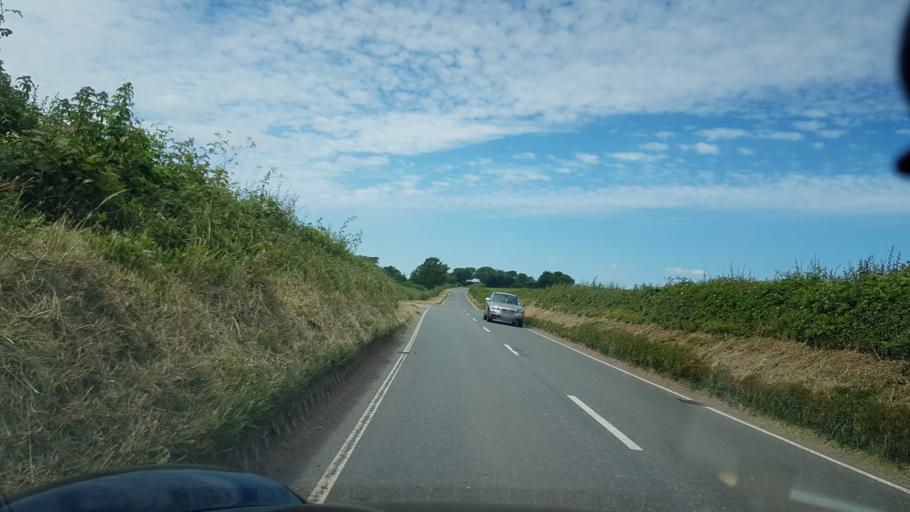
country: GB
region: Wales
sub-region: Carmarthenshire
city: Whitland
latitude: 51.7684
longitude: -4.5883
